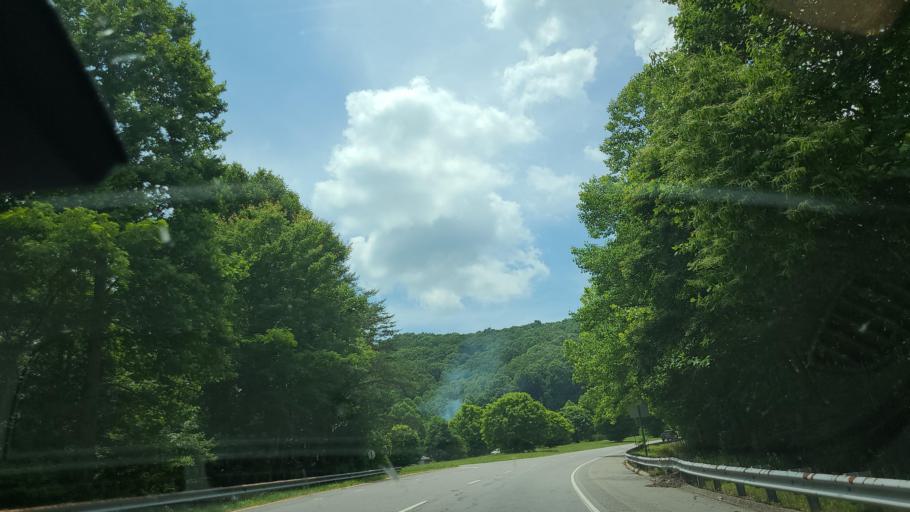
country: US
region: Georgia
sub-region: Fannin County
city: McCaysville
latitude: 35.0137
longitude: -84.2796
